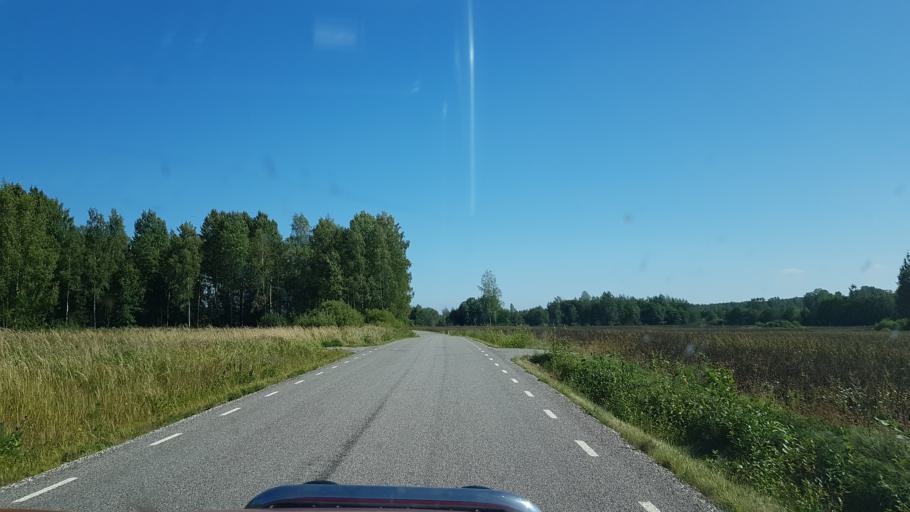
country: EE
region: Polvamaa
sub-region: Polva linn
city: Polva
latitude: 58.2115
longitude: 27.1721
